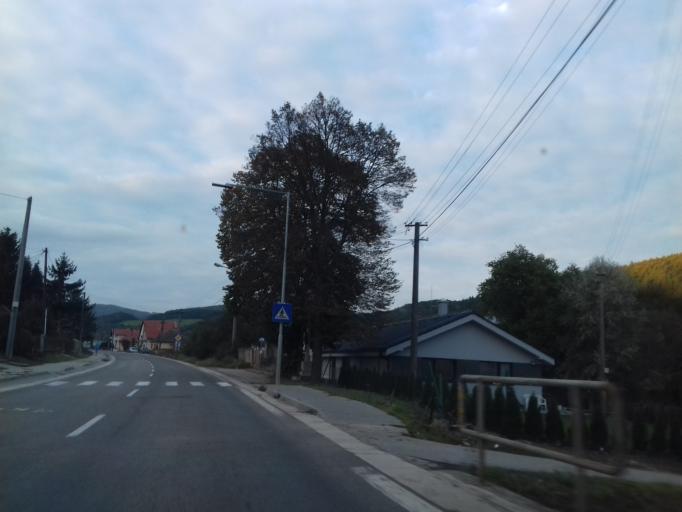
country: SK
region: Trenciansky
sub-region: Okres Trencin
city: Trencin
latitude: 48.9014
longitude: 17.9527
